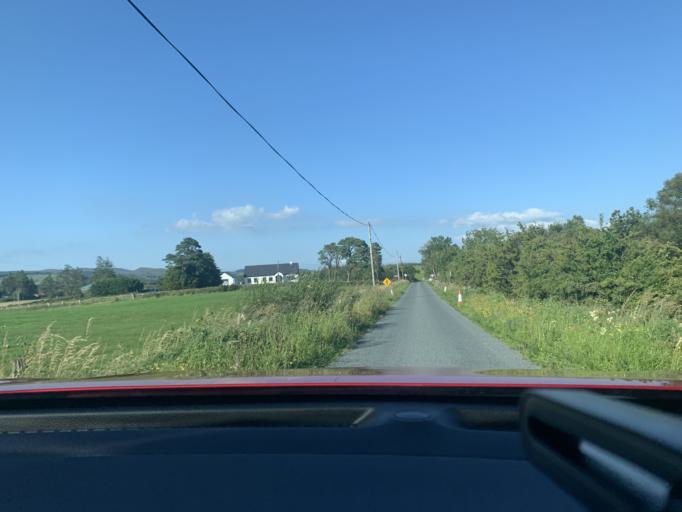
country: IE
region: Connaught
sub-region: Sligo
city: Tobercurry
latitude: 54.1489
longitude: -8.6744
